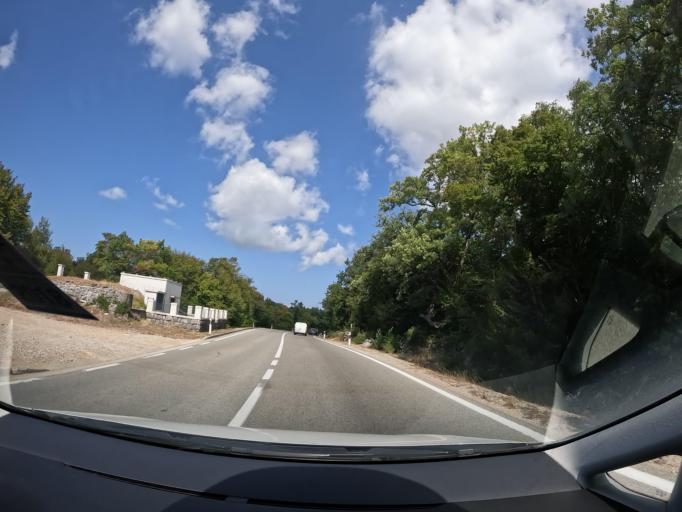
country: HR
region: Primorsko-Goranska
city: Njivice
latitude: 45.0882
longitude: 14.5407
